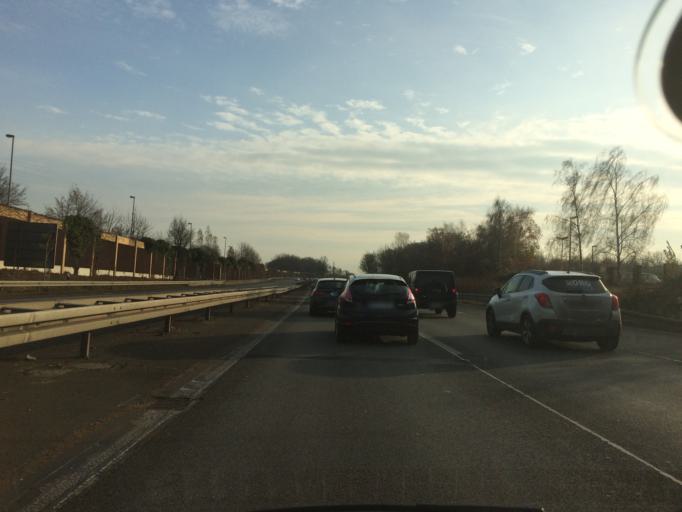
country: DE
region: North Rhine-Westphalia
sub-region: Regierungsbezirk Dusseldorf
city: Oberhausen
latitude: 51.5043
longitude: 6.8597
